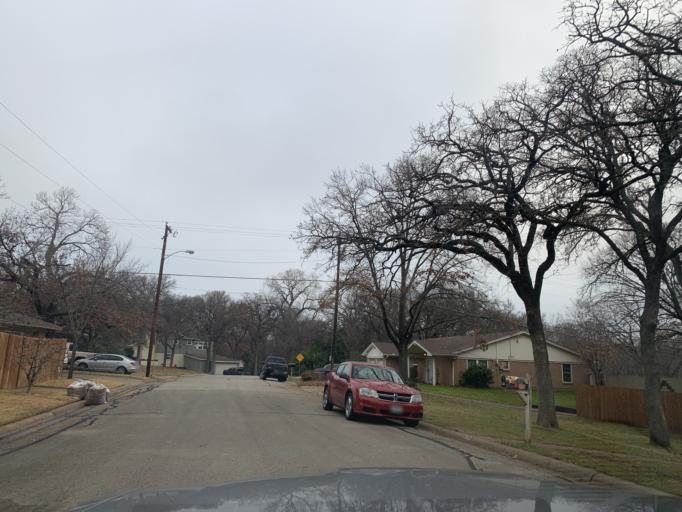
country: US
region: Texas
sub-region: Tarrant County
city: Bedford
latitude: 32.8300
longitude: -97.1516
